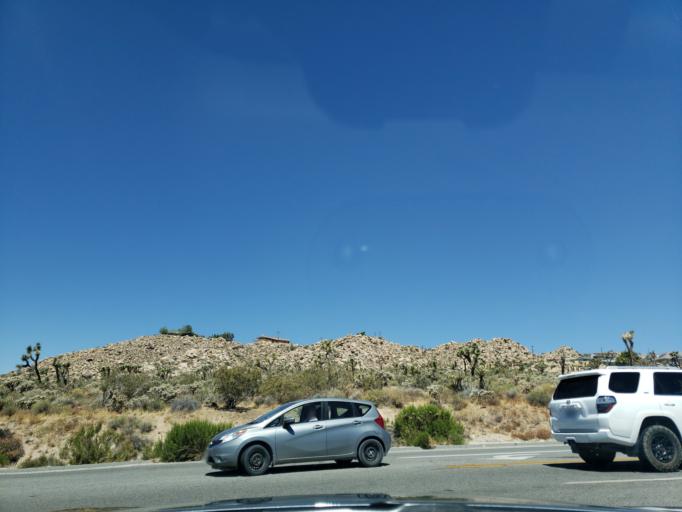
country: US
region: California
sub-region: San Bernardino County
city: Yucca Valley
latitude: 34.1351
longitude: -116.4124
